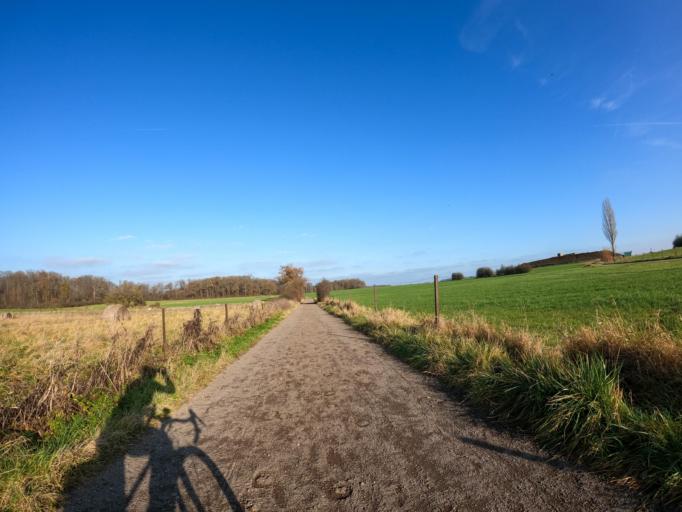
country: LU
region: Luxembourg
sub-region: Canton de Capellen
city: Kehlen
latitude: 49.6770
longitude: 6.0188
